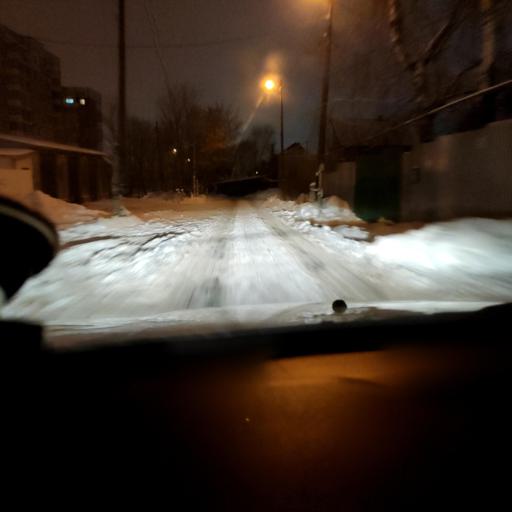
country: RU
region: Samara
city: Petra-Dubrava
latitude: 53.3002
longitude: 50.2727
